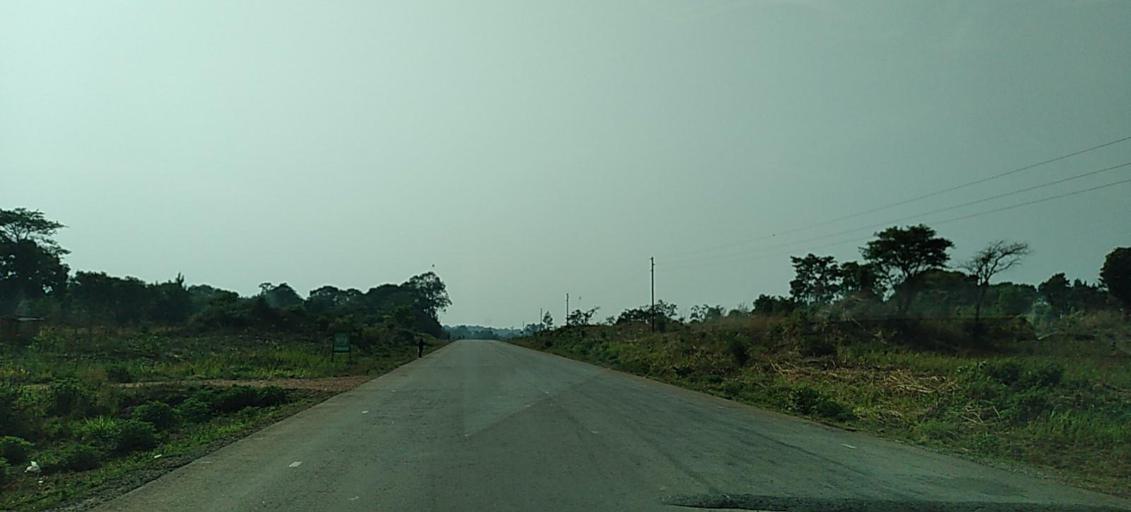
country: ZM
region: North-Western
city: Kansanshi
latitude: -12.3114
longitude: 26.9419
